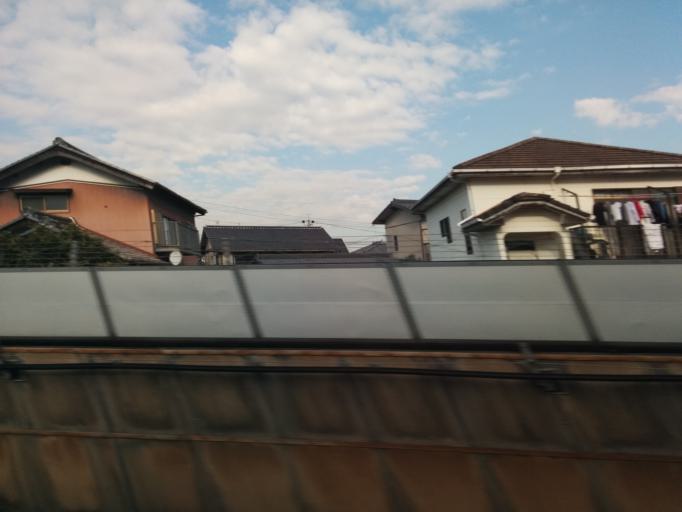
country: JP
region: Aichi
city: Obu
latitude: 35.0252
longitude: 136.9845
